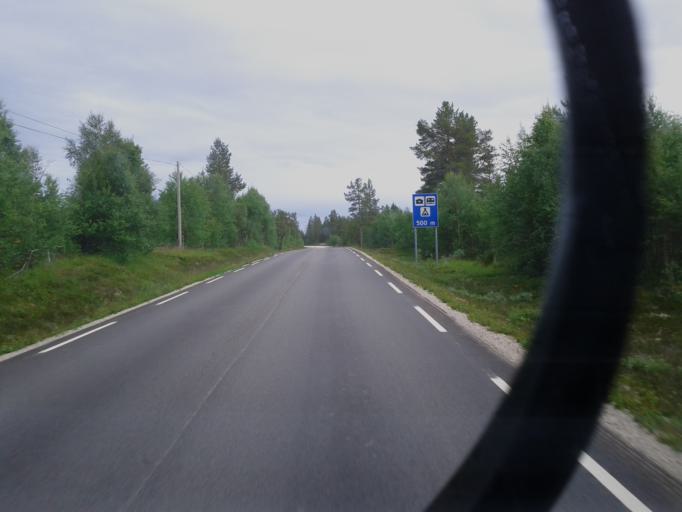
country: NO
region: Hedmark
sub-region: Engerdal
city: Engerdal
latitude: 62.0530
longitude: 11.6869
